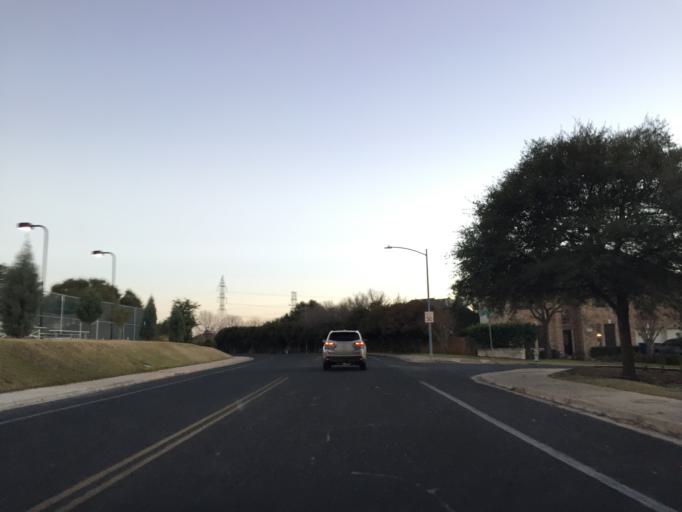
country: US
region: Texas
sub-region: Williamson County
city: Jollyville
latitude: 30.4032
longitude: -97.7683
